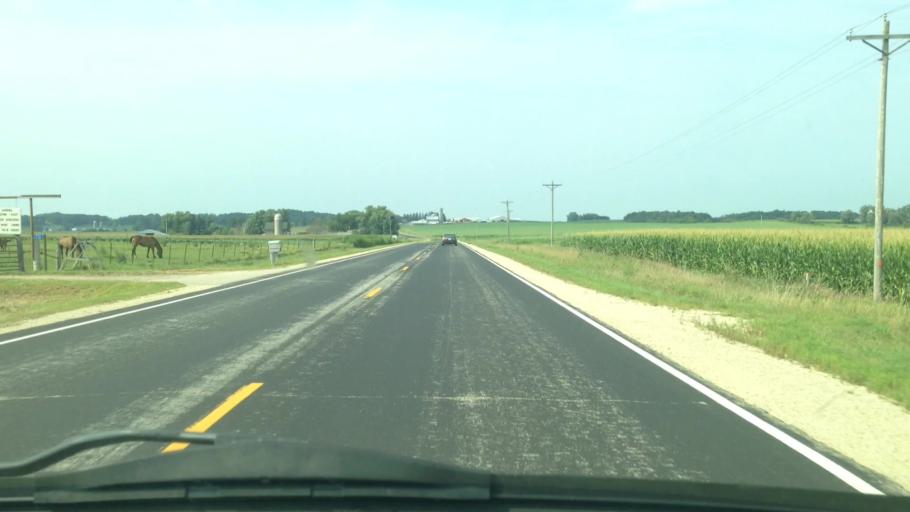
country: US
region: Minnesota
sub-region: Winona County
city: Lewiston
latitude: 43.9454
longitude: -91.9549
